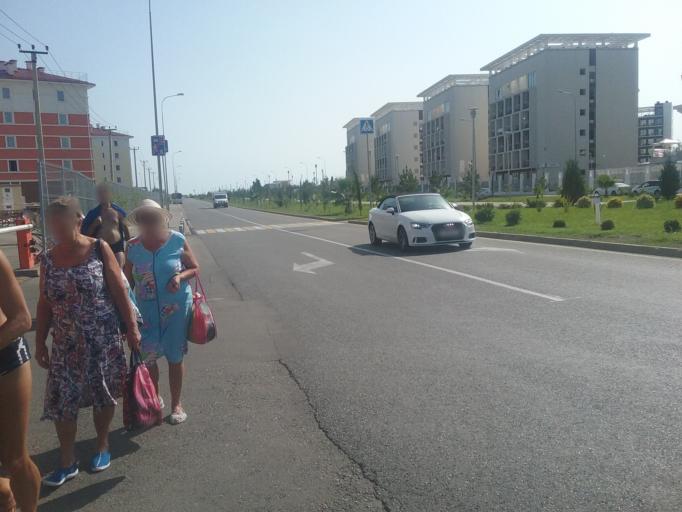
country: RU
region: Krasnodarskiy
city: Vysokoye
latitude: 43.3908
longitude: 39.9908
